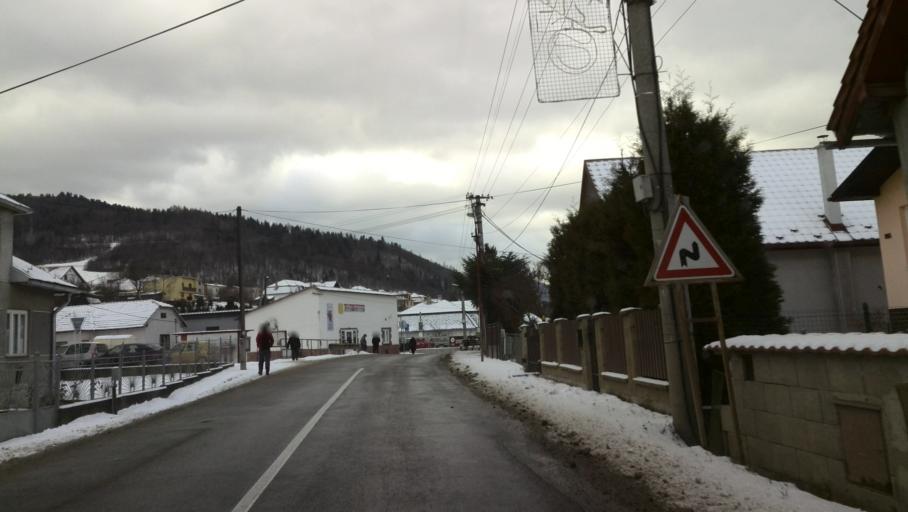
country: SK
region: Kosicky
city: Gelnica
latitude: 48.8738
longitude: 20.9924
